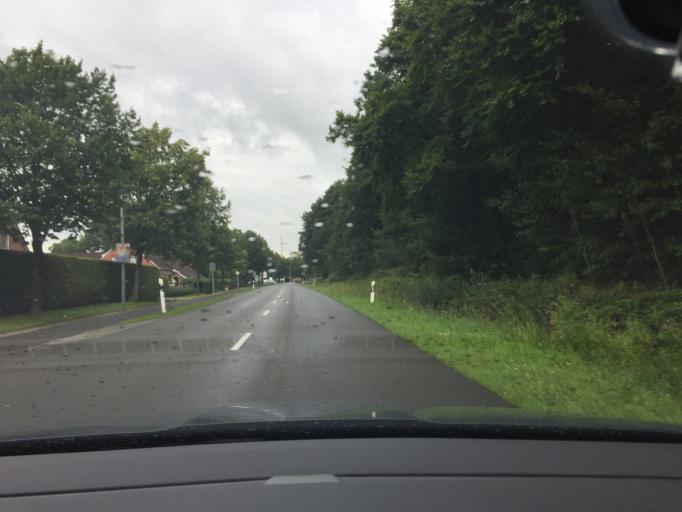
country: DE
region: Lower Saxony
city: Aurich
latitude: 53.4044
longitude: 7.4398
